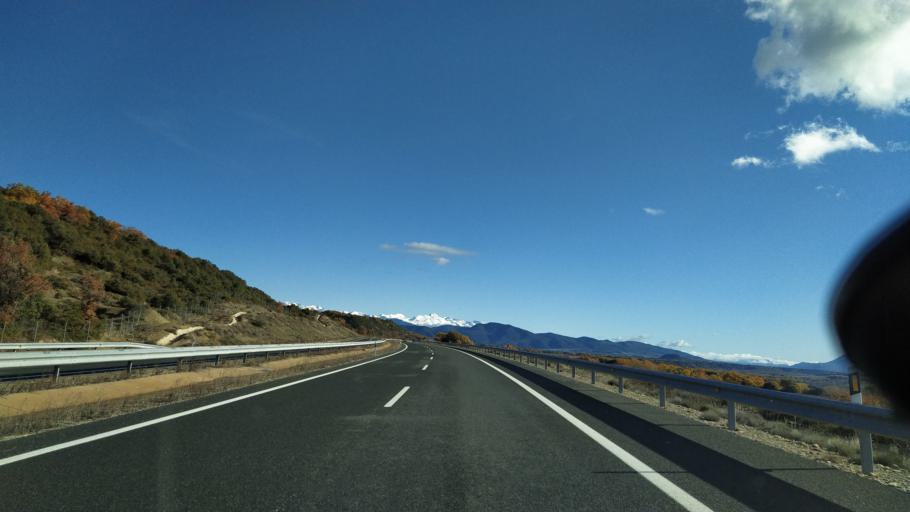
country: ES
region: Aragon
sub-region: Provincia de Zaragoza
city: Artieda
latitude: 42.6087
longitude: -0.9712
